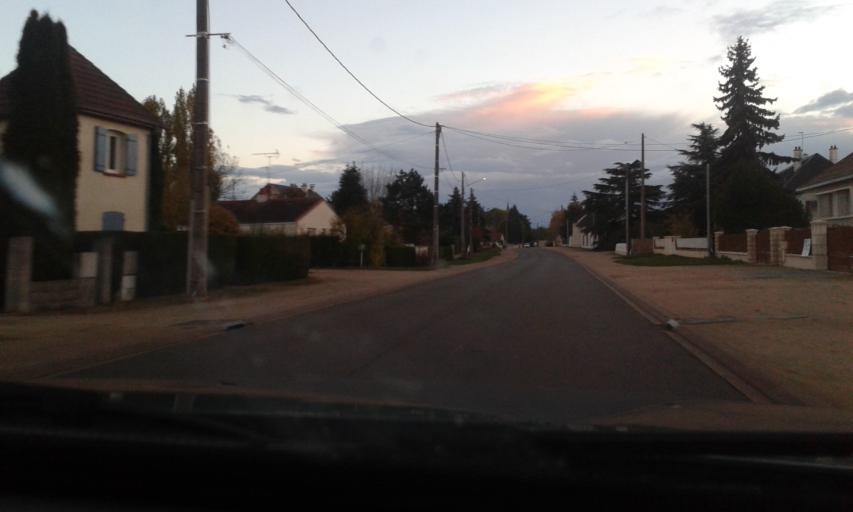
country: FR
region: Centre
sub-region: Departement du Loiret
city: Huisseau-sur-Mauves
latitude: 47.8983
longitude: 1.7044
